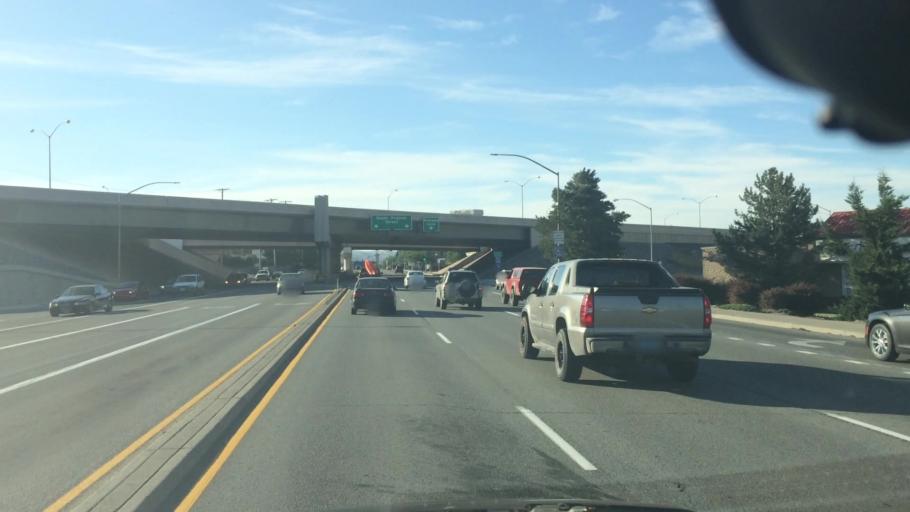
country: US
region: Nevada
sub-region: Washoe County
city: Reno
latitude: 39.4775
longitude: -119.7894
